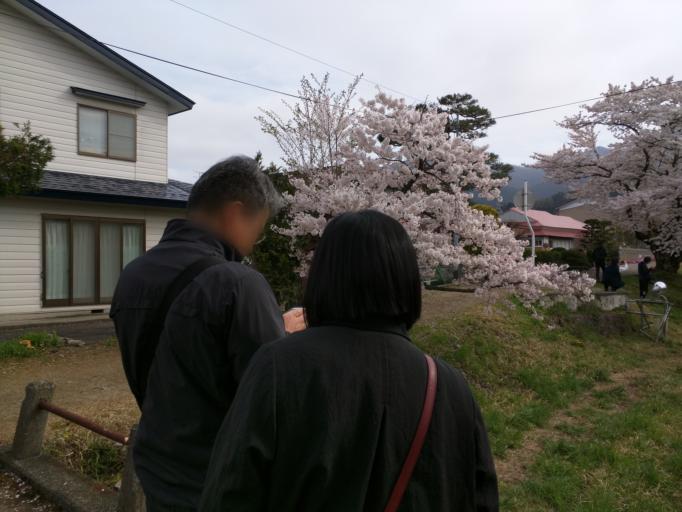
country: JP
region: Fukushima
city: Inawashiro
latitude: 37.5377
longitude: 140.1385
